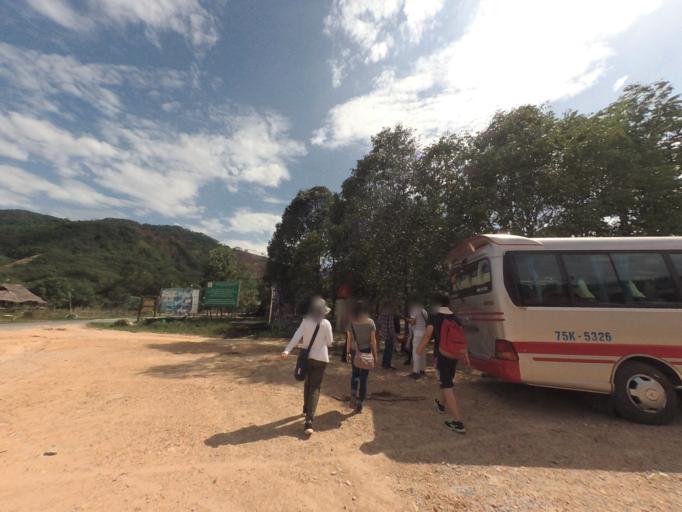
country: VN
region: Thua Thien-Hue
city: A Luoi
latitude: 16.3006
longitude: 107.3254
